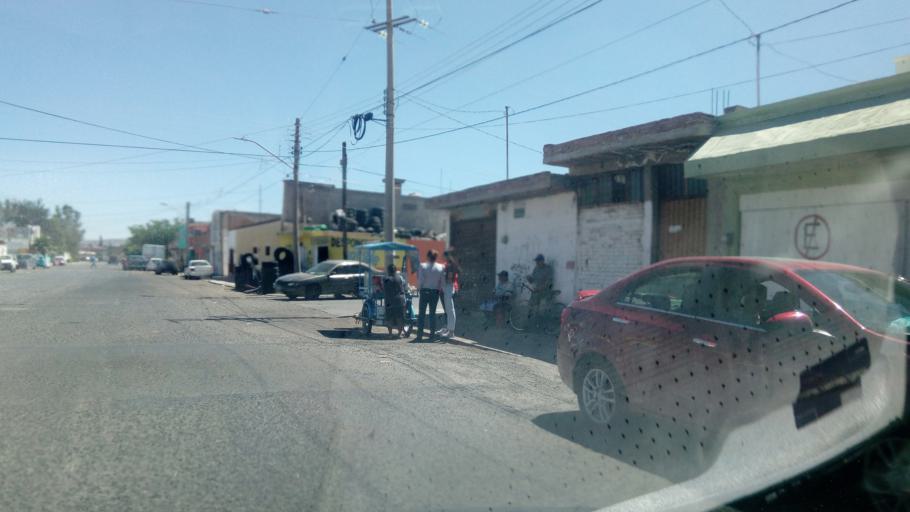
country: MX
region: Durango
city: Victoria de Durango
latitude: 24.0168
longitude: -104.6574
